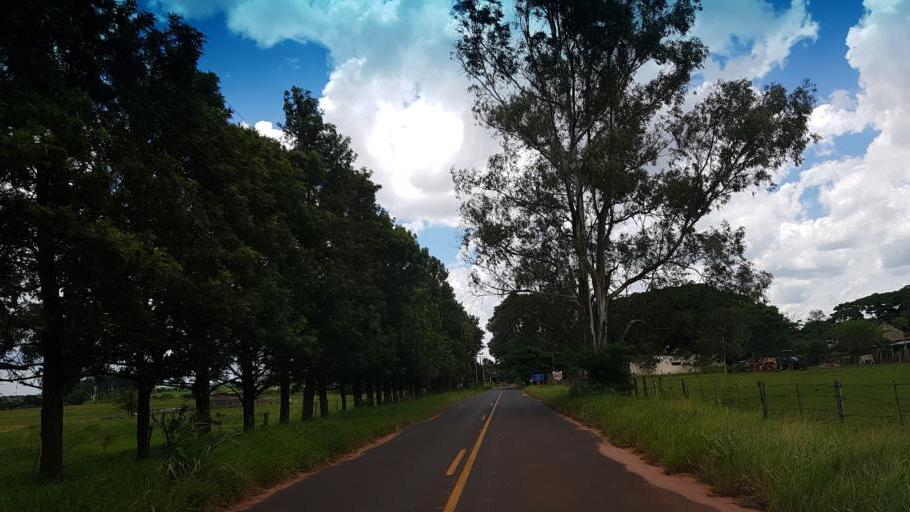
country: BR
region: Sao Paulo
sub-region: Paraguacu Paulista
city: Paraguacu Paulista
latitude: -22.3545
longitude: -50.6249
